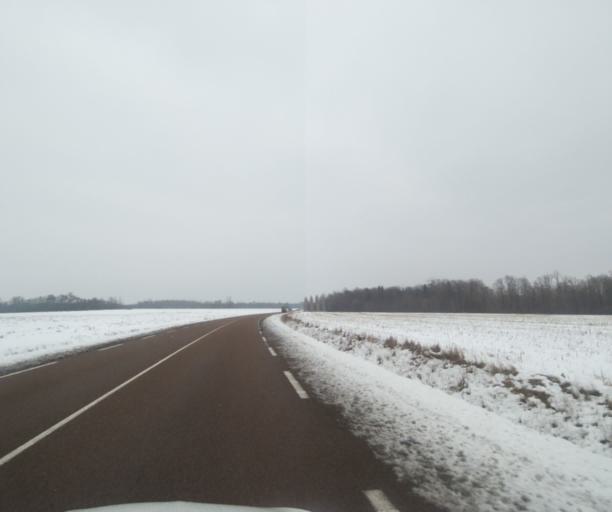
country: FR
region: Champagne-Ardenne
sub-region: Departement de la Haute-Marne
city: Saint-Dizier
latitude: 48.5950
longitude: 4.8923
